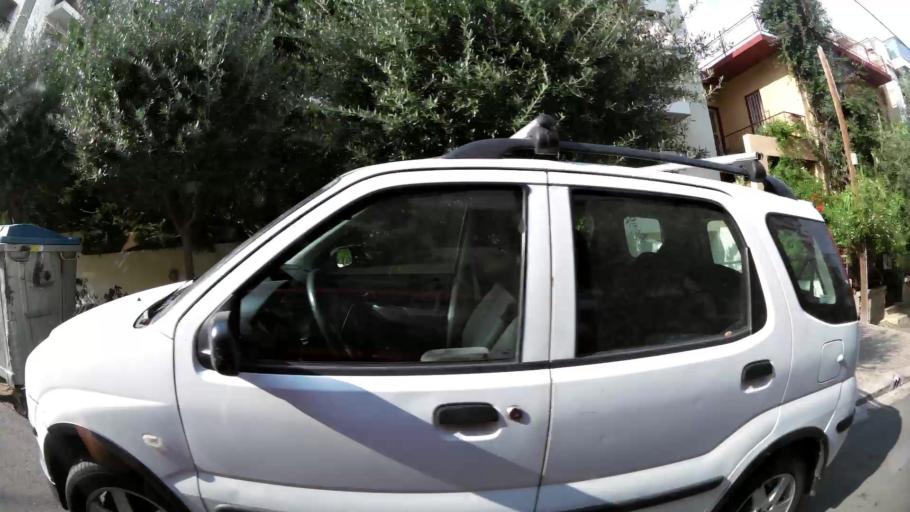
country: GR
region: Attica
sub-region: Nomarchia Athinas
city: Nea Smyrni
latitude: 37.9410
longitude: 23.7177
